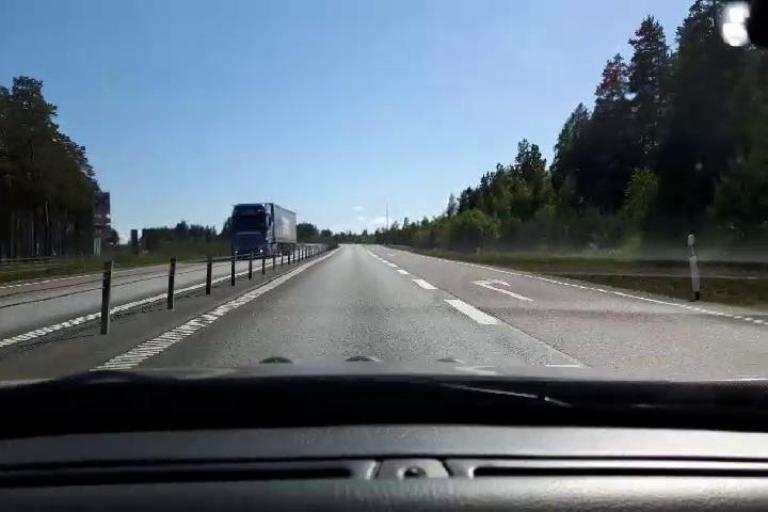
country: SE
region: Gaevleborg
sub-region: Gavle Kommun
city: Norrsundet
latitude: 61.0765
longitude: 16.9673
